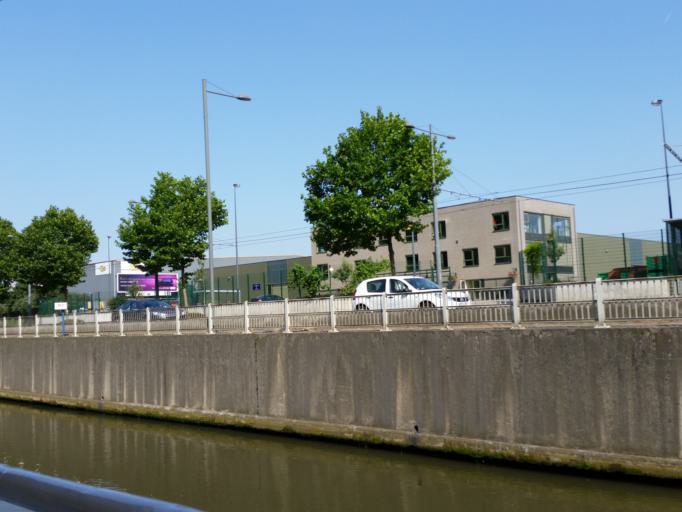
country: BE
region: Brussels Capital
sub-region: Bruxelles-Capitale
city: Brussels
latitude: 50.8771
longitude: 4.3650
